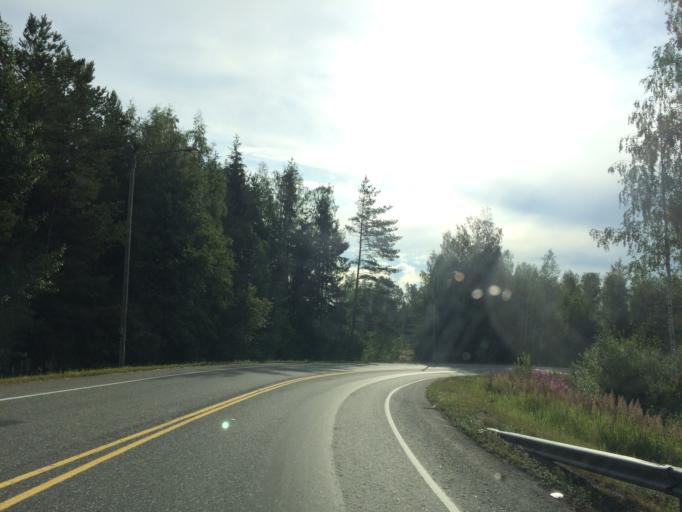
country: FI
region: Haeme
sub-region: Haemeenlinna
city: Janakkala
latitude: 60.9149
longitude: 24.5491
